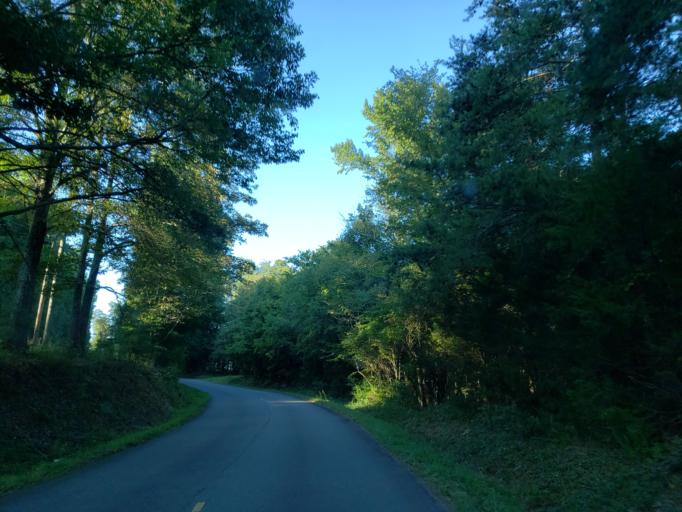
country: US
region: Georgia
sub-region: Bartow County
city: Rydal
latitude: 34.3045
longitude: -84.7325
